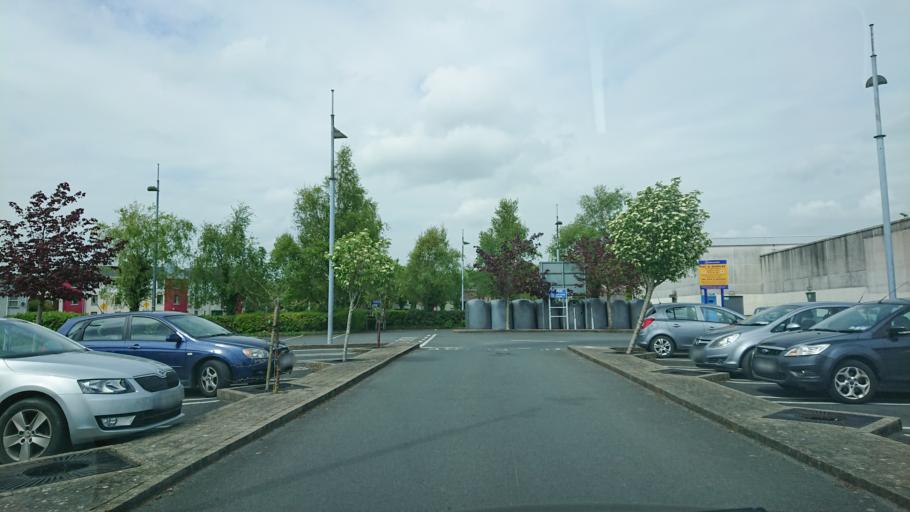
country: IE
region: Munster
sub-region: Waterford
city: Waterford
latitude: 52.2533
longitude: -7.1112
